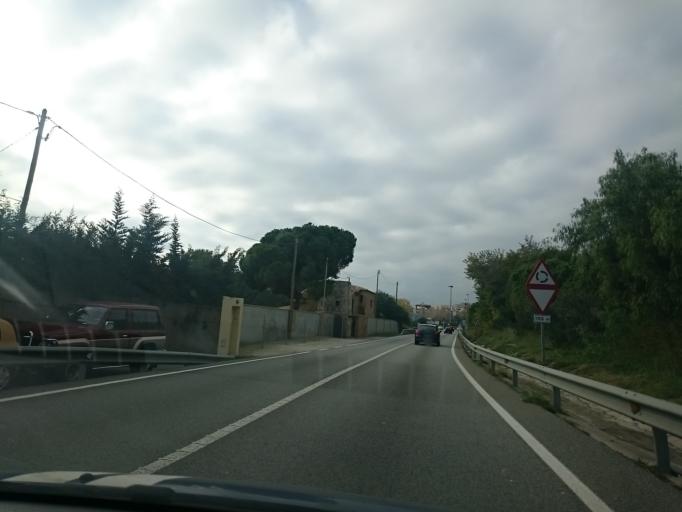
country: ES
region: Catalonia
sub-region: Provincia de Barcelona
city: Sitges
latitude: 41.2388
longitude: 1.8257
